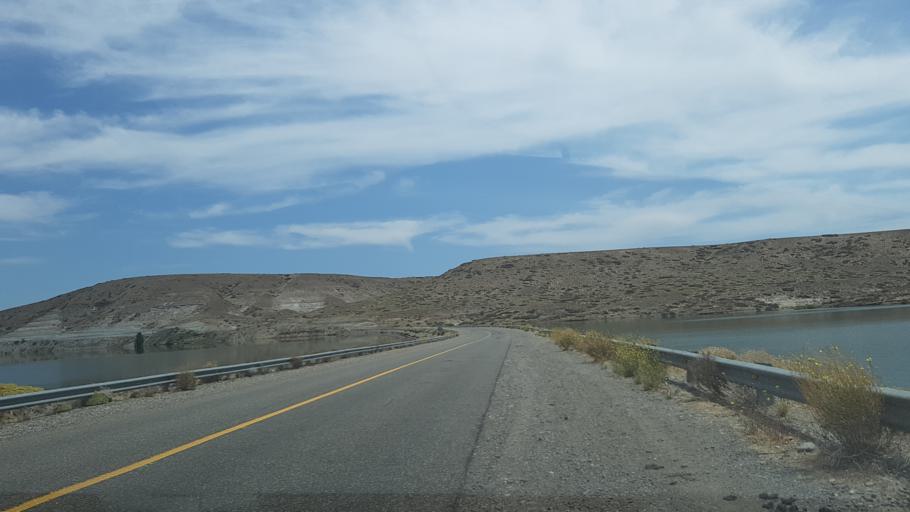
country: AR
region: Neuquen
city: Junin de los Andes
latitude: -40.4372
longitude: -70.6531
